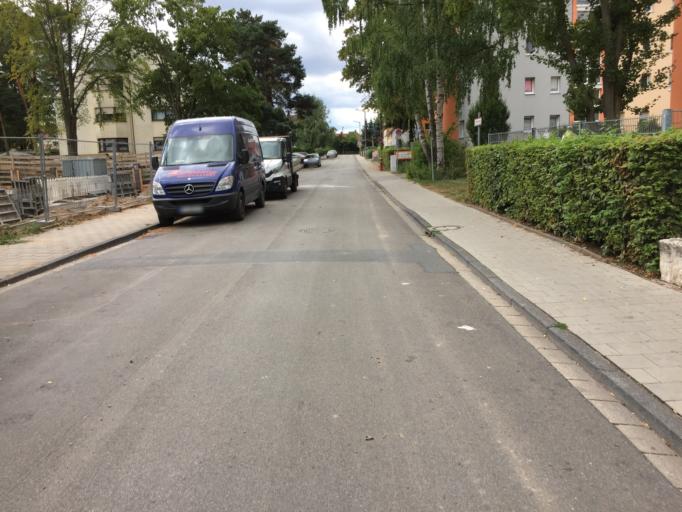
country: DE
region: Bavaria
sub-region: Regierungsbezirk Mittelfranken
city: Erlangen
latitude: 49.5670
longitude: 11.0042
